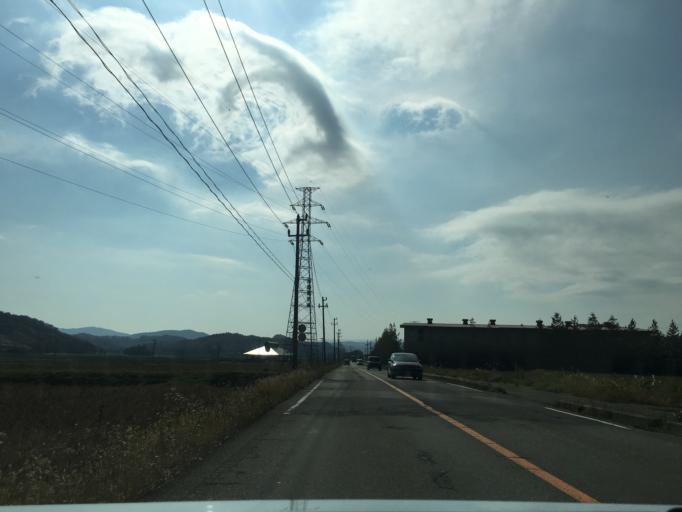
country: JP
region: Fukushima
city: Inawashiro
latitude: 37.4790
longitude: 140.0108
